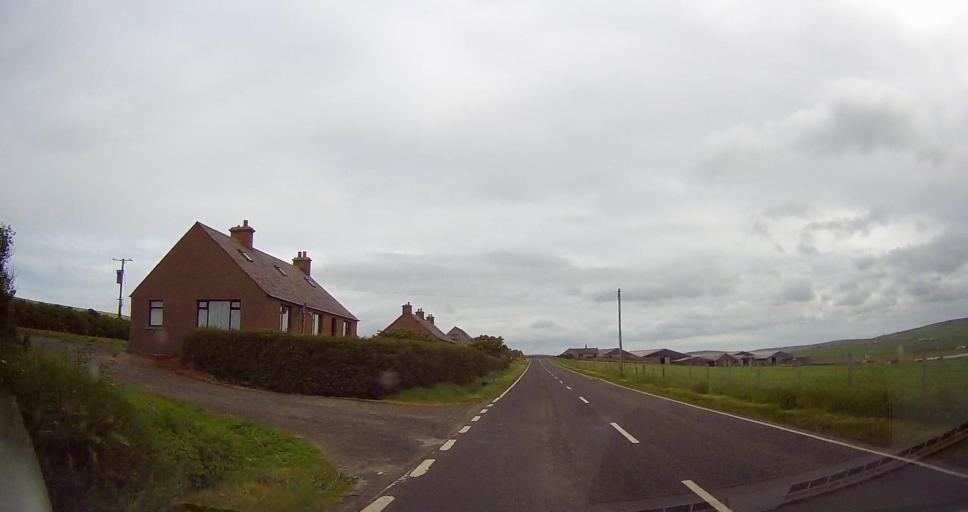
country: GB
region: Scotland
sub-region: Orkney Islands
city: Stromness
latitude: 58.9782
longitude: -3.2695
